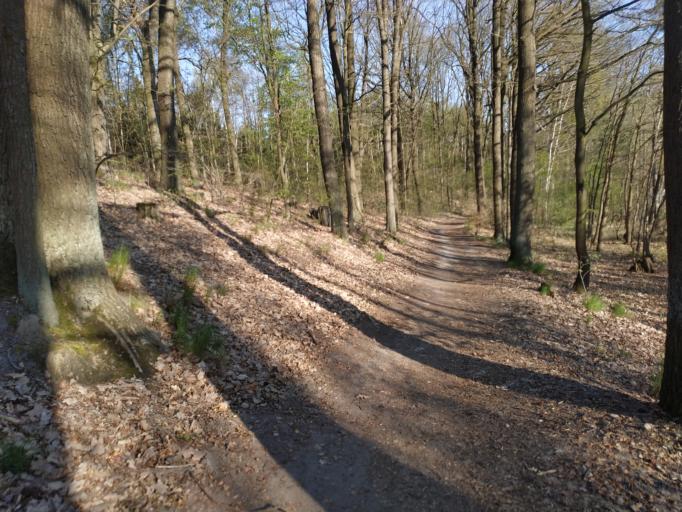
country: DE
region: Brandenburg
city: Strausberg
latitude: 52.5662
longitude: 13.8352
